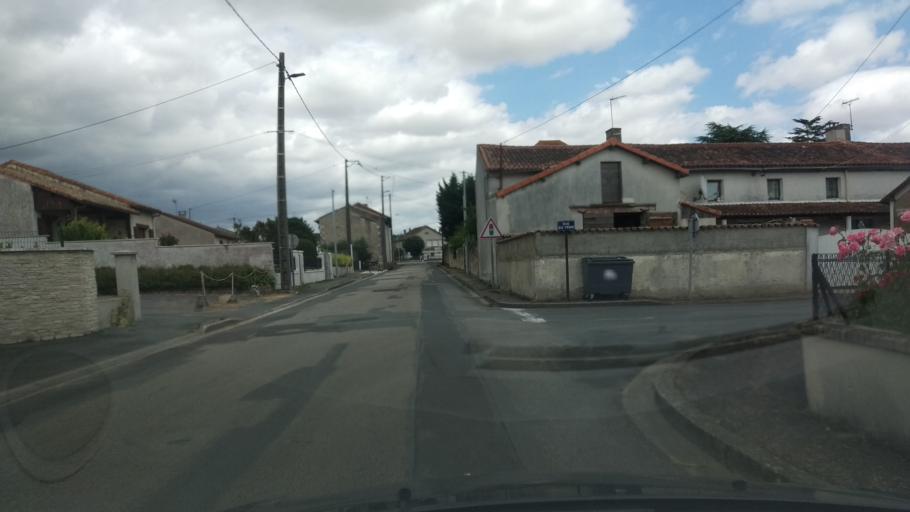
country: FR
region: Poitou-Charentes
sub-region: Departement de la Vienne
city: Vouille
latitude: 46.6454
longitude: 0.1692
